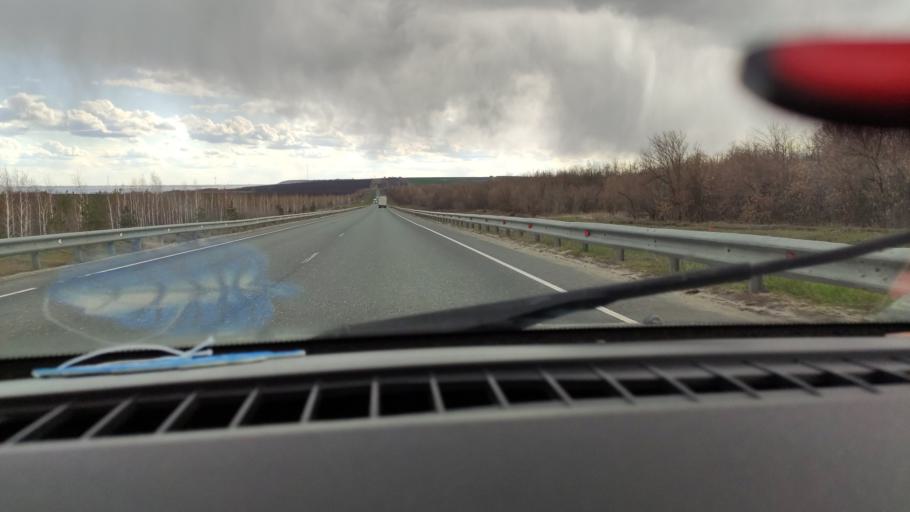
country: RU
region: Saratov
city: Balakovo
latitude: 52.1515
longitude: 47.8119
